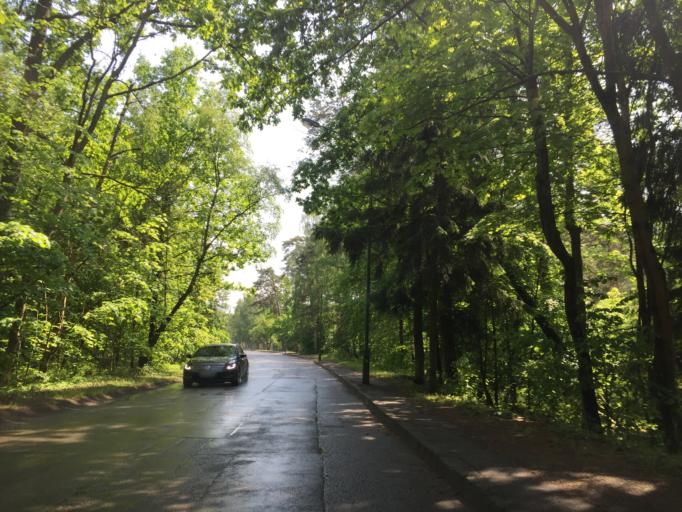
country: LT
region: Klaipedos apskritis
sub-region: Klaipeda
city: Klaipeda
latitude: 55.7704
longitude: 21.0839
